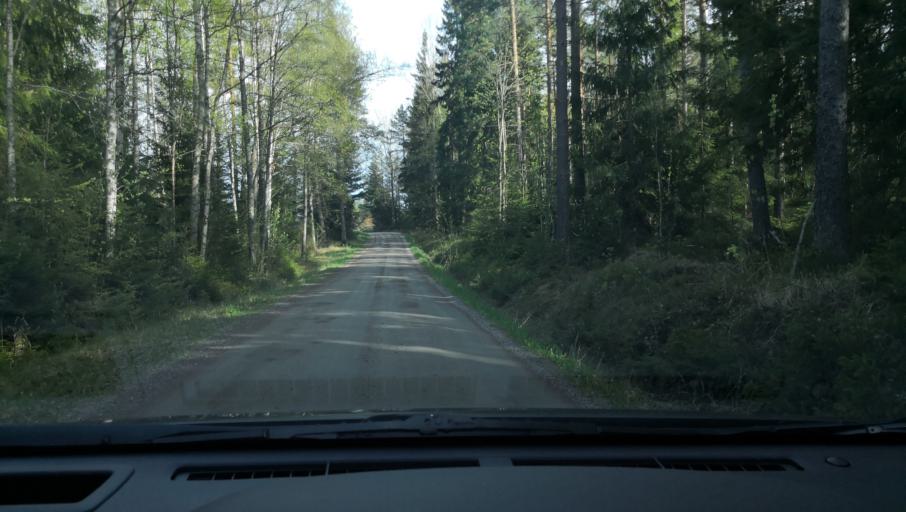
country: SE
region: OErebro
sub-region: Askersunds Kommun
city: Asbro
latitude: 59.0303
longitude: 15.0493
